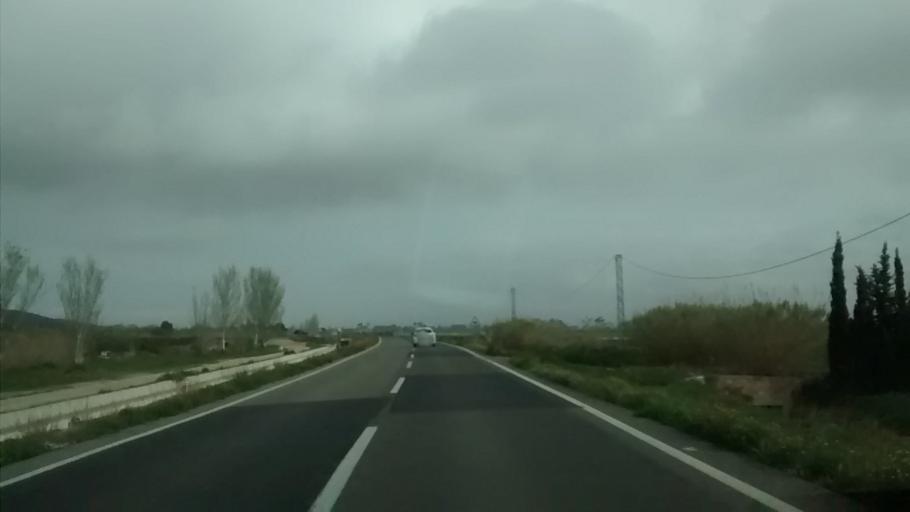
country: ES
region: Catalonia
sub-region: Provincia de Tarragona
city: Sant Carles de la Rapita
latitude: 40.6398
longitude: 0.6012
